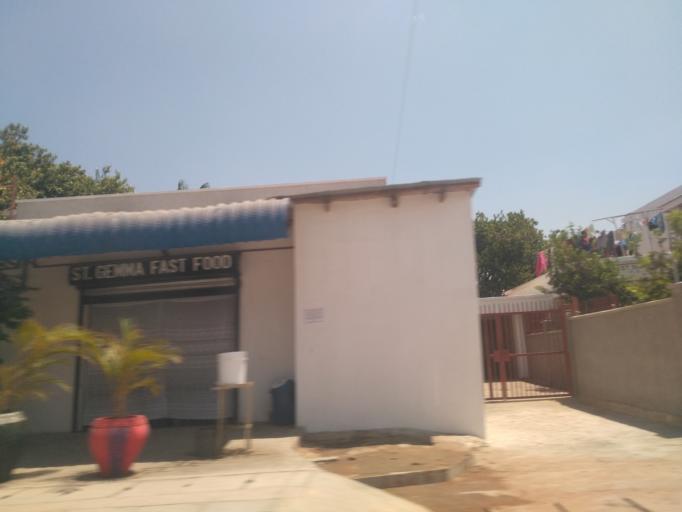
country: TZ
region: Dodoma
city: Dodoma
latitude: -6.1777
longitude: 35.7495
